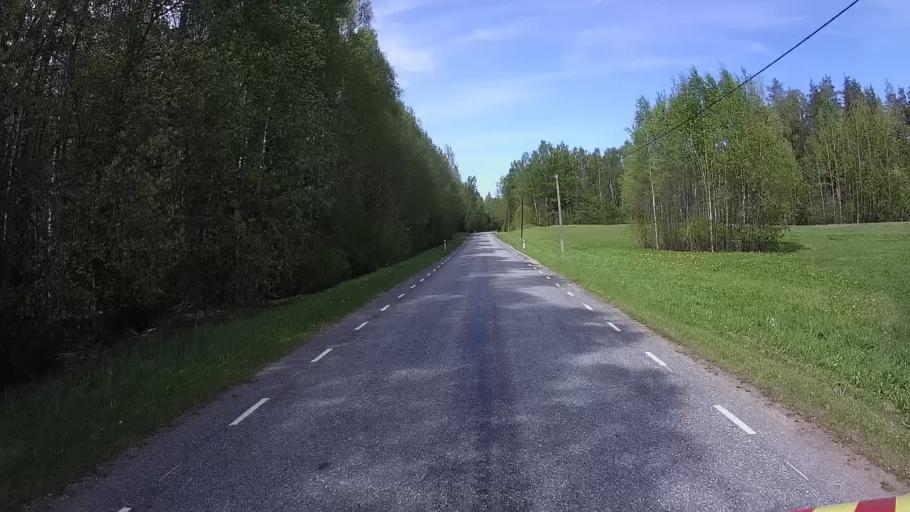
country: EE
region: Valgamaa
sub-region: Valga linn
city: Valga
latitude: 57.6653
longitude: 26.2872
